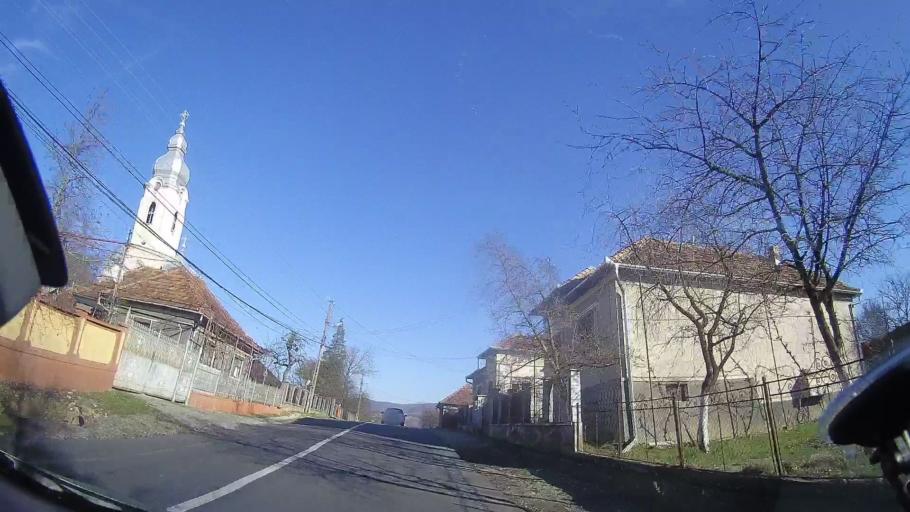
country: RO
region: Bihor
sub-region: Comuna Bratca
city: Beznea
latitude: 46.9559
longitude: 22.6135
